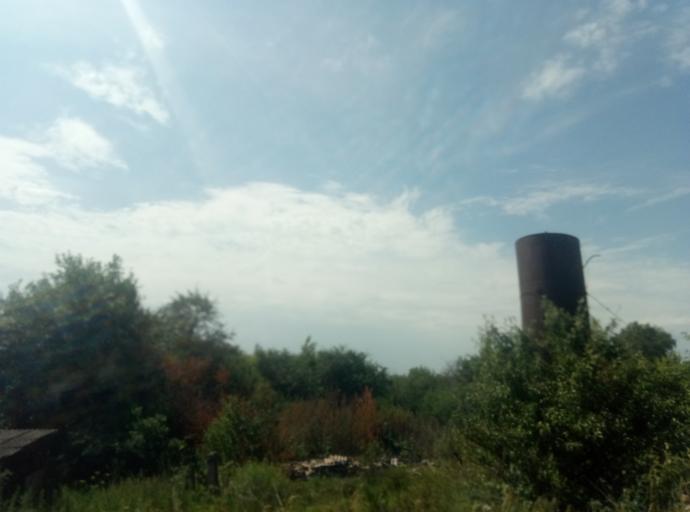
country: RU
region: Tula
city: Kireyevsk
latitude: 53.9207
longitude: 37.9540
